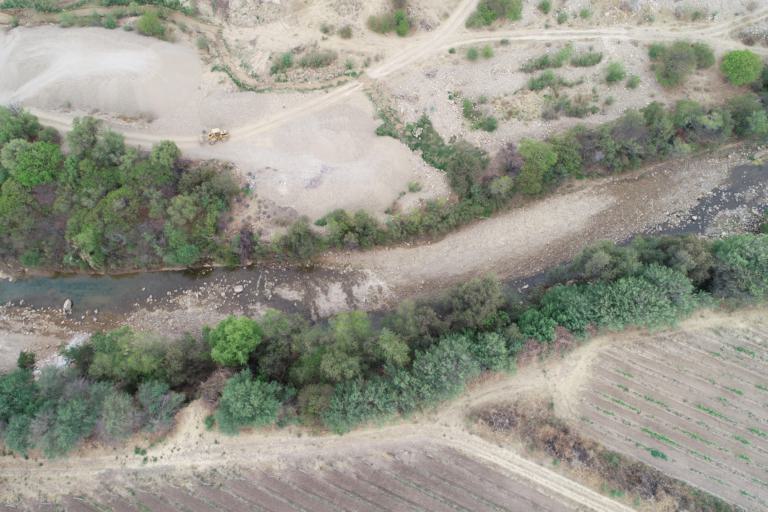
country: BO
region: Tarija
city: Tarija
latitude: -21.6014
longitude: -64.6206
